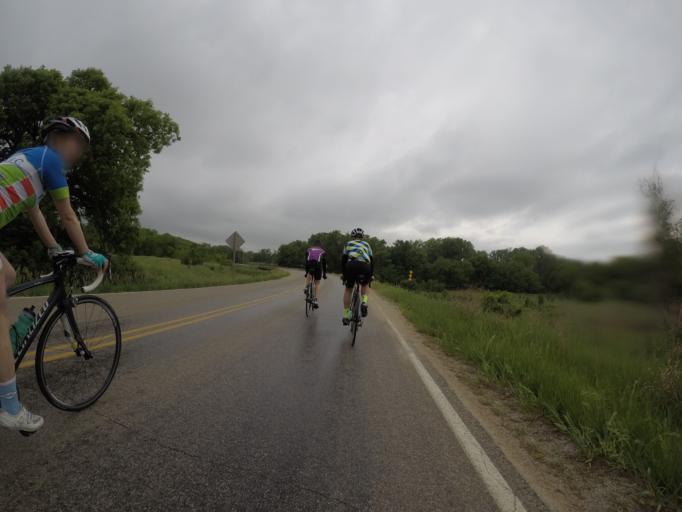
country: US
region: Kansas
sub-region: Pottawatomie County
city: Westmoreland
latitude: 39.4786
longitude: -96.1826
